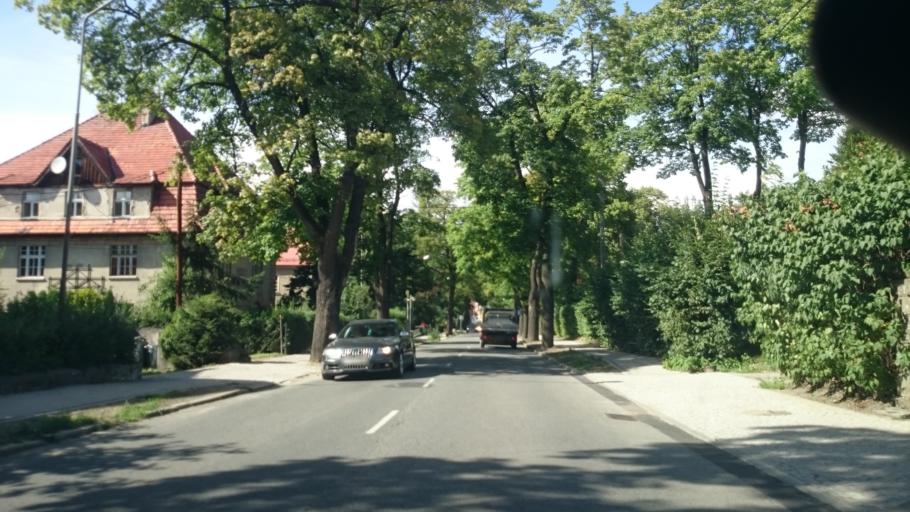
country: PL
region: Lower Silesian Voivodeship
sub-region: Powiat klodzki
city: Polanica-Zdroj
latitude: 50.4021
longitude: 16.5133
